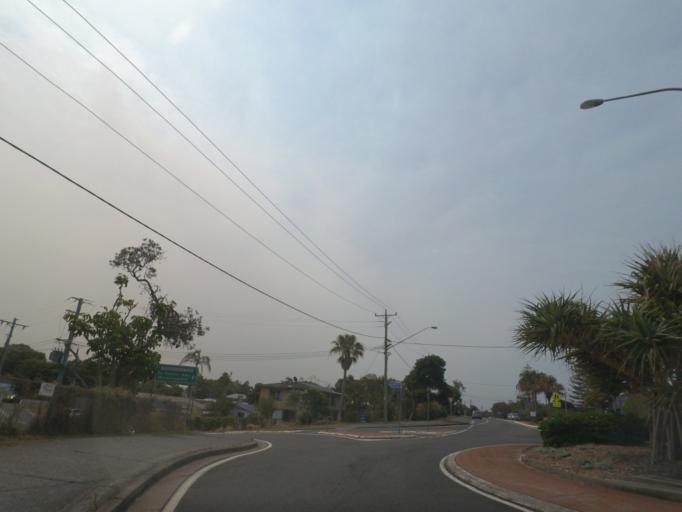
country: AU
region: New South Wales
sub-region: Tweed
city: Casuarina
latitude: -28.3307
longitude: 153.5691
